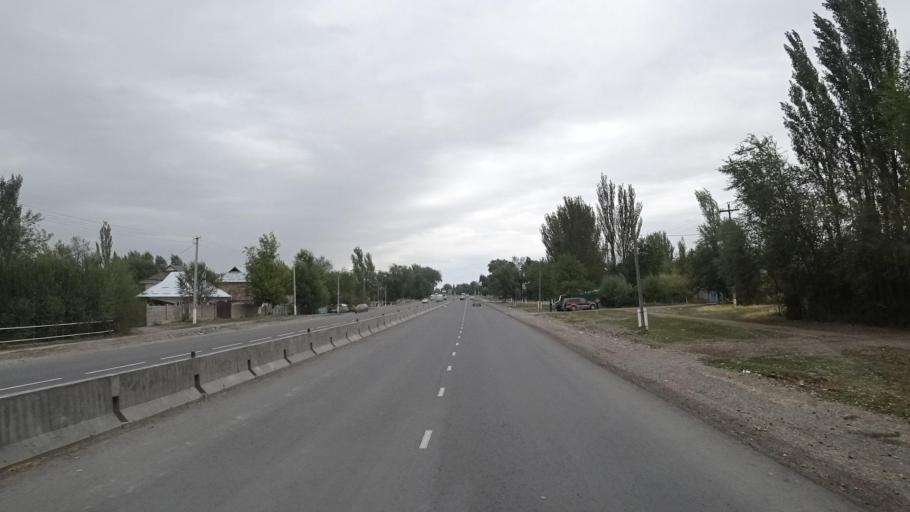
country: KG
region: Chuy
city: Kara-Balta
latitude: 42.8351
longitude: 73.9125
